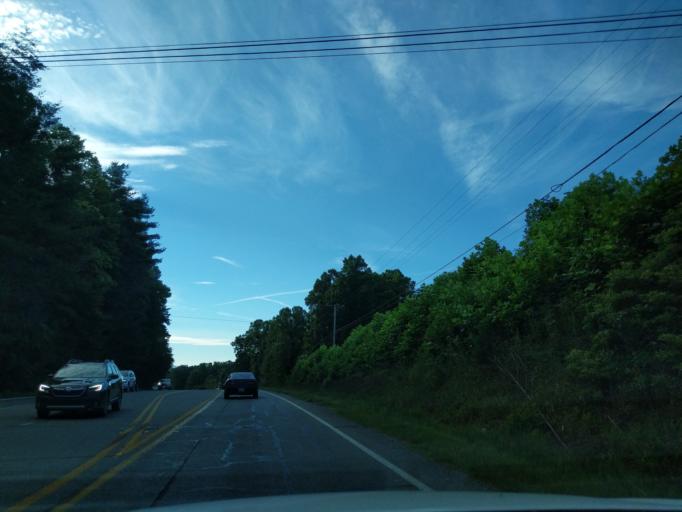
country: US
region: Georgia
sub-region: Fannin County
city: Blue Ridge
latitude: 34.9035
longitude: -84.3735
